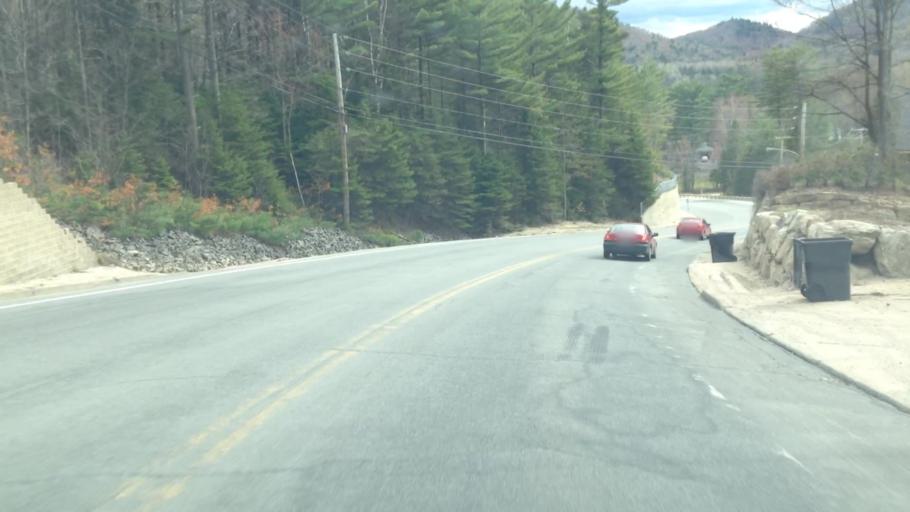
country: CA
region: Quebec
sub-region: Laurentides
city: Sainte-Adele
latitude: 45.9873
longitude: -74.1189
